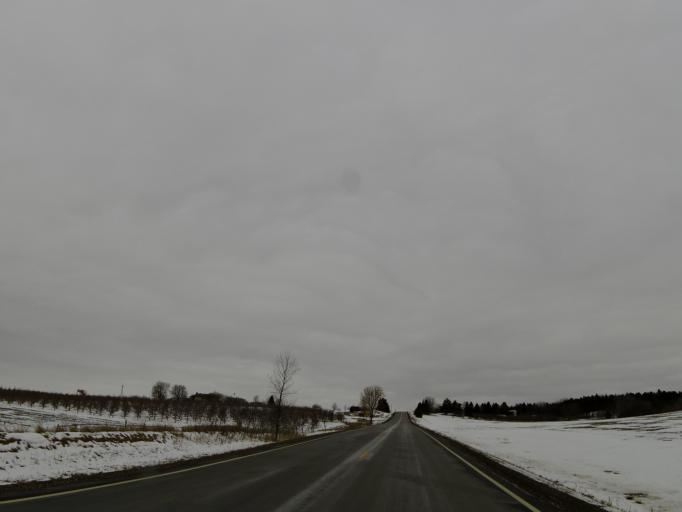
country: US
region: Wisconsin
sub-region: Pierce County
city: Prescott
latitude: 44.7901
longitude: -92.8122
